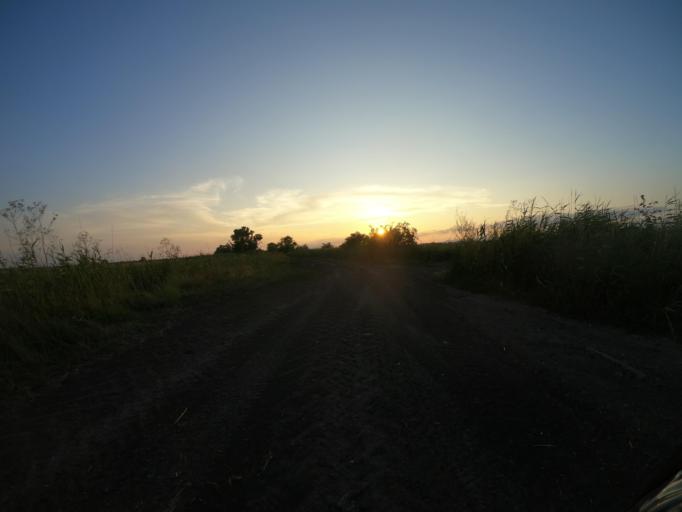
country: HU
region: Borsod-Abauj-Zemplen
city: Szentistvan
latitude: 47.7465
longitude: 20.7473
